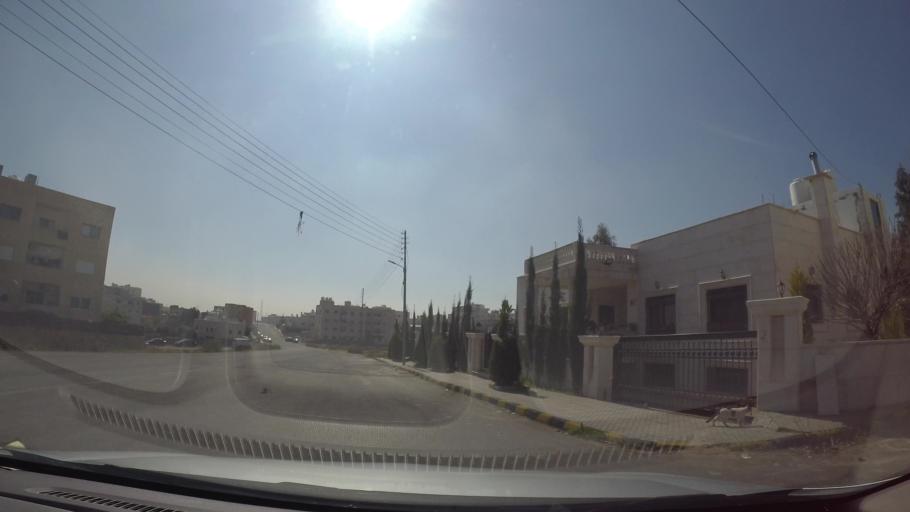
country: JO
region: Amman
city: Al Bunayyat ash Shamaliyah
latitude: 31.8951
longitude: 35.8949
